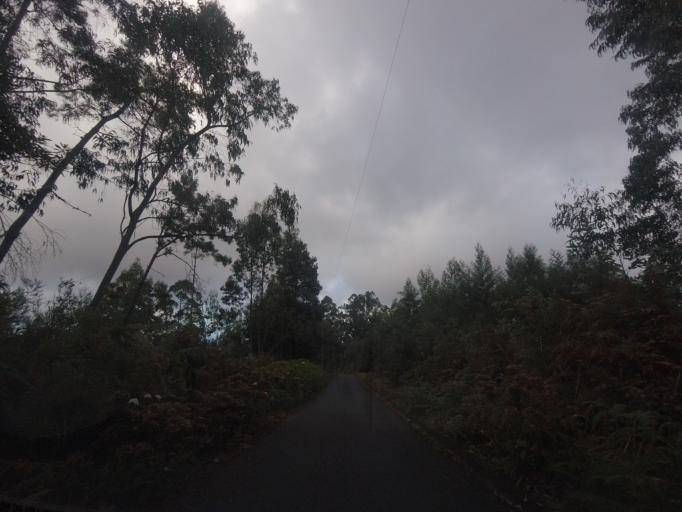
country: PT
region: Madeira
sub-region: Santana
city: Santana
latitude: 32.7965
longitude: -16.8915
